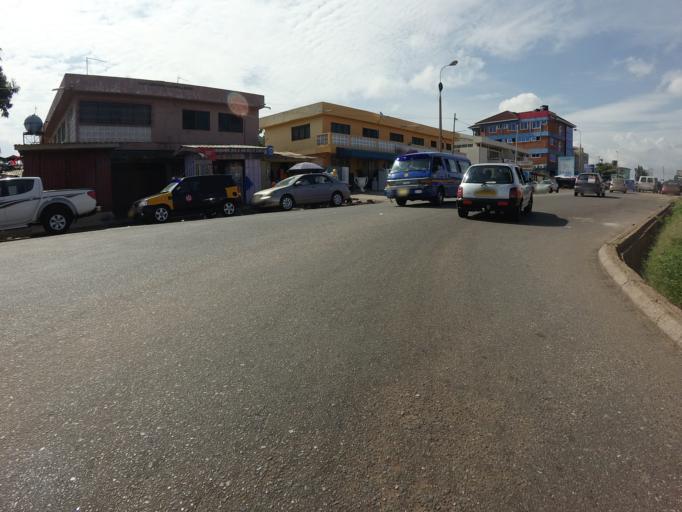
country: GH
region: Greater Accra
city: Accra
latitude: 5.5966
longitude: -0.1950
